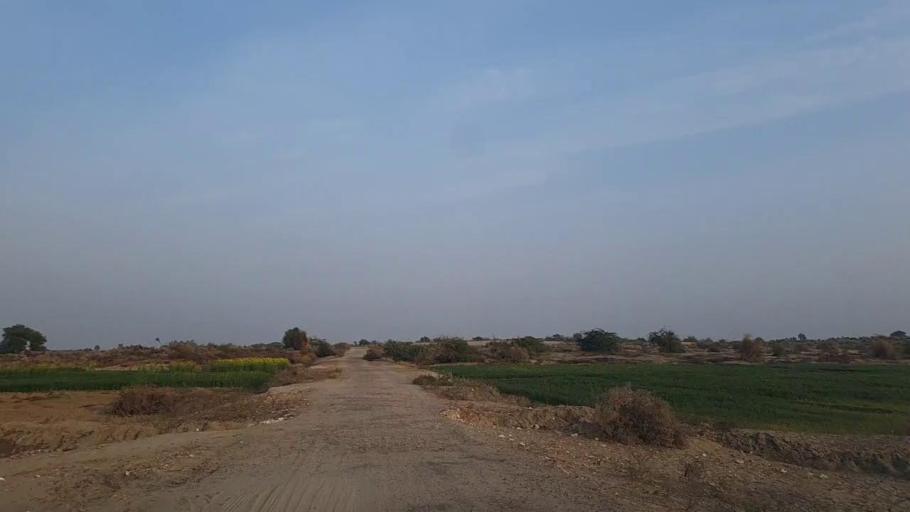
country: PK
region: Sindh
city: Jam Sahib
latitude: 26.4076
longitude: 68.5944
